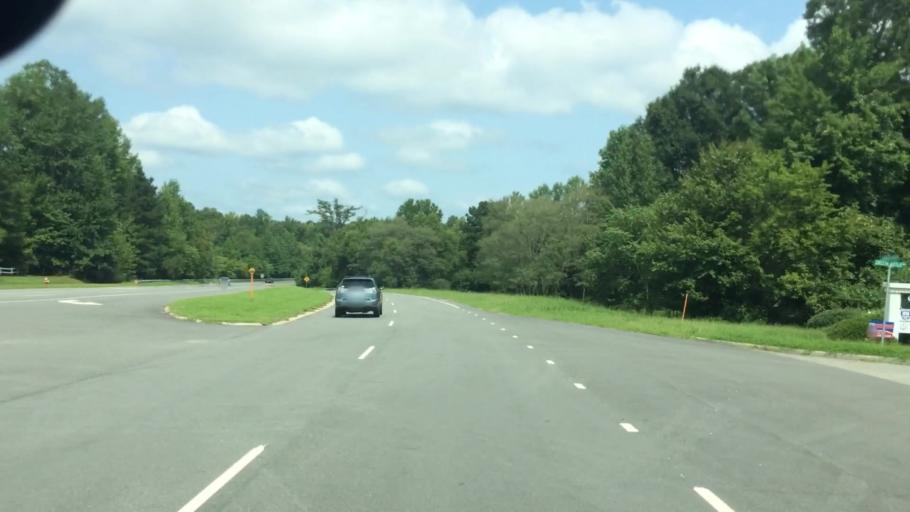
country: US
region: Virginia
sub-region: James City County
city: Williamsburg
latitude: 37.2558
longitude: -76.7870
